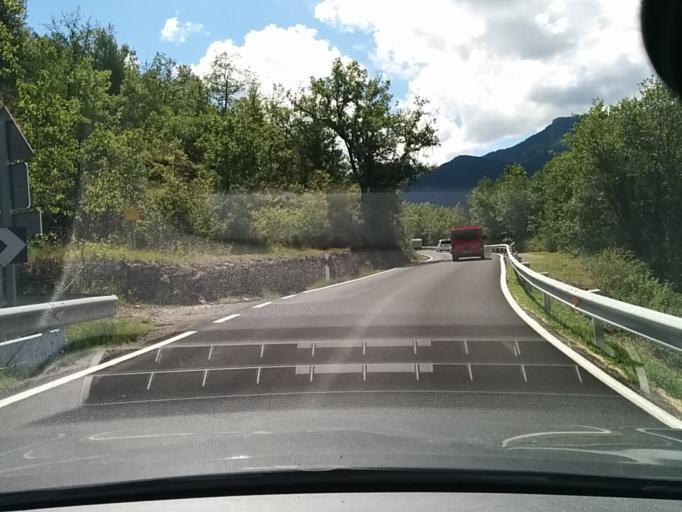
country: ES
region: Aragon
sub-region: Provincia de Huesca
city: Fiscal
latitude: 42.4859
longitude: -0.0843
